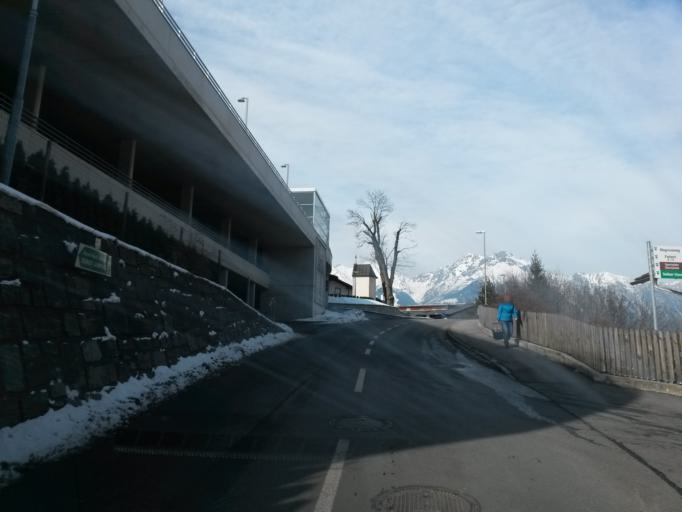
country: AT
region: Tyrol
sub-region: Politischer Bezirk Imst
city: Arzl im Pitztal
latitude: 47.2068
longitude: 10.7626
